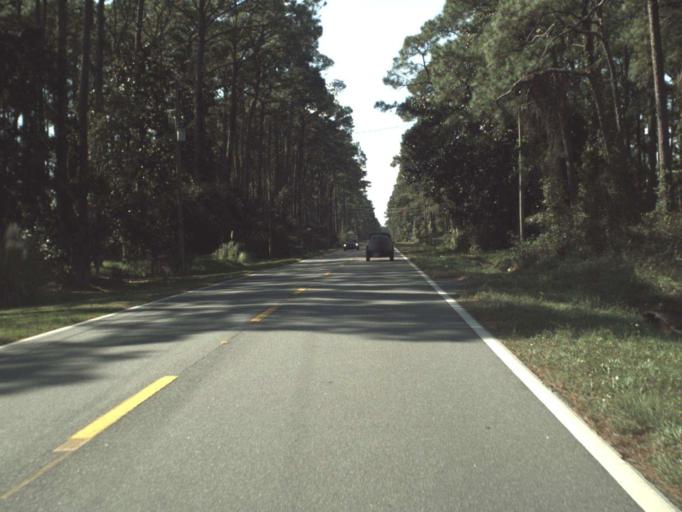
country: US
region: Florida
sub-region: Franklin County
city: Carrabelle
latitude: 29.8971
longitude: -84.5593
